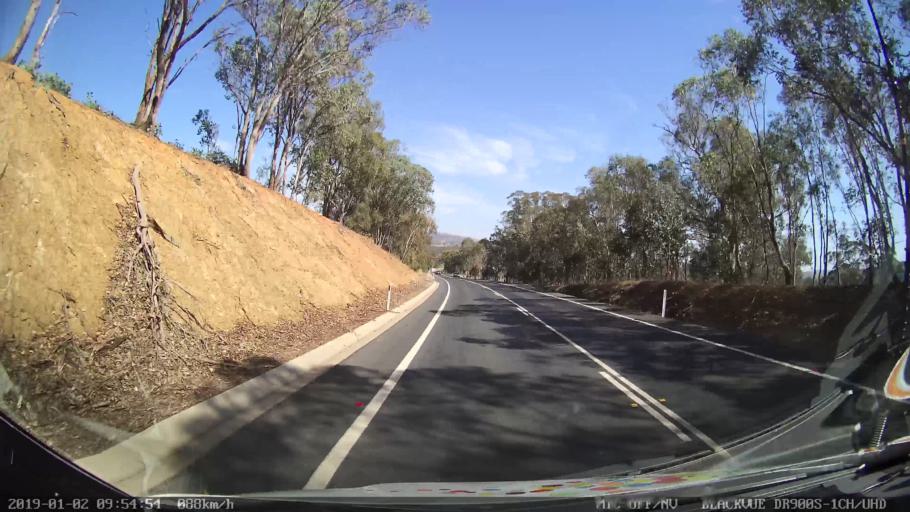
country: AU
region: New South Wales
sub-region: Tumut Shire
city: Tumut
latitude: -35.2292
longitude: 148.1942
